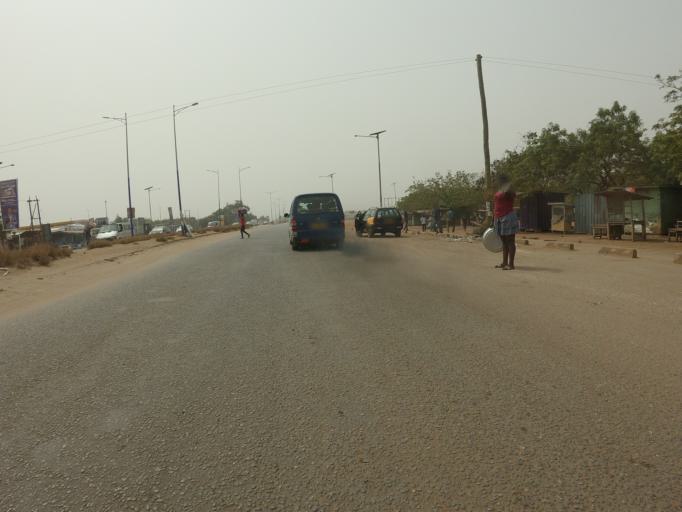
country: GH
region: Greater Accra
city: Tema
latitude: 5.7160
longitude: 0.0145
